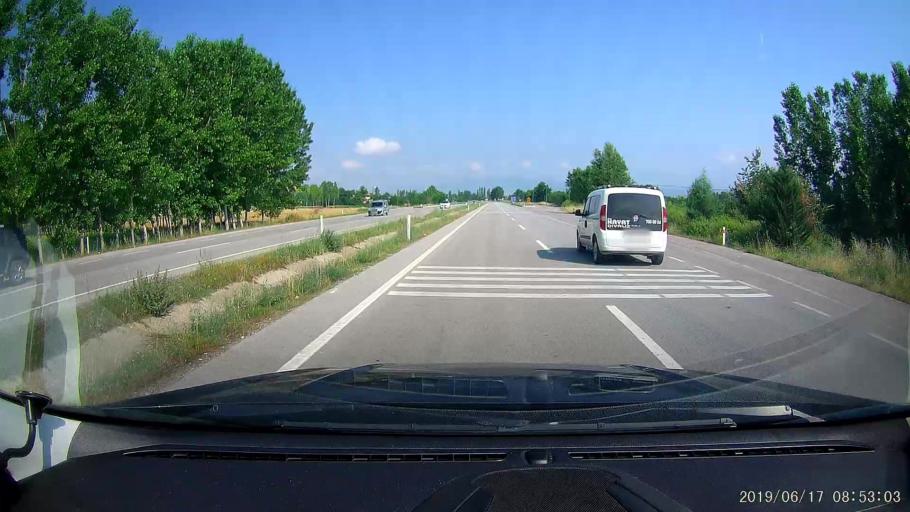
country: TR
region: Tokat
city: Erbaa
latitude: 40.7055
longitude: 36.4874
